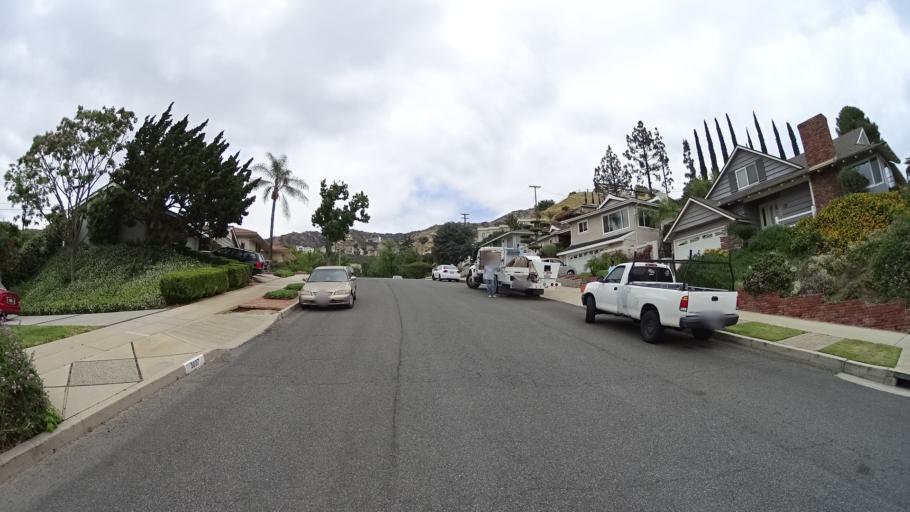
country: US
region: California
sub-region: Los Angeles County
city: Burbank
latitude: 34.2120
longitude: -118.3320
